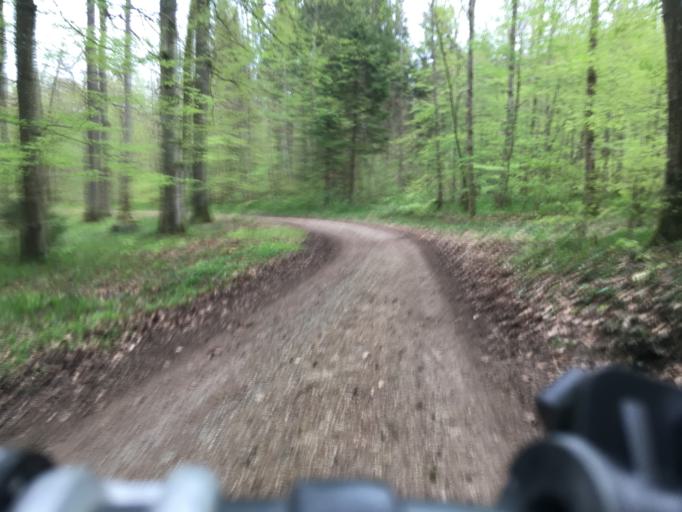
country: DE
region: Baden-Wuerttemberg
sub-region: Freiburg Region
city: Gailingen
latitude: 47.7142
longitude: 8.7380
